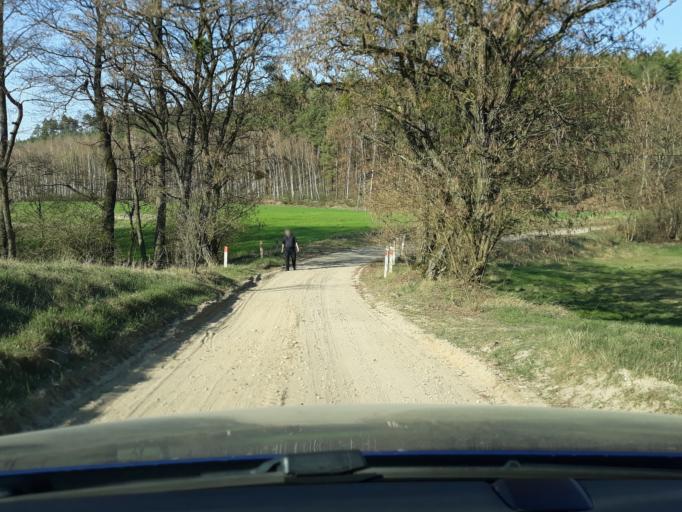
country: PL
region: Pomeranian Voivodeship
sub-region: Powiat bytowski
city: Lipnica
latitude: 53.9121
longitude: 17.4321
